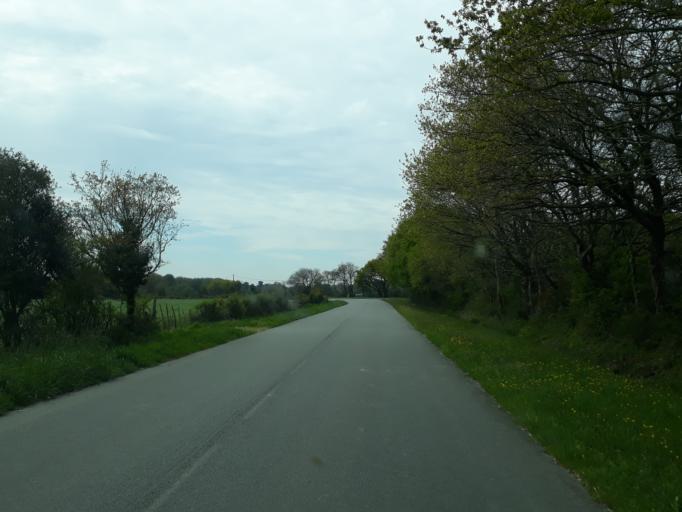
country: FR
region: Pays de la Loire
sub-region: Departement de la Loire-Atlantique
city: Saint-Molf
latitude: 47.3699
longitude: -2.4097
